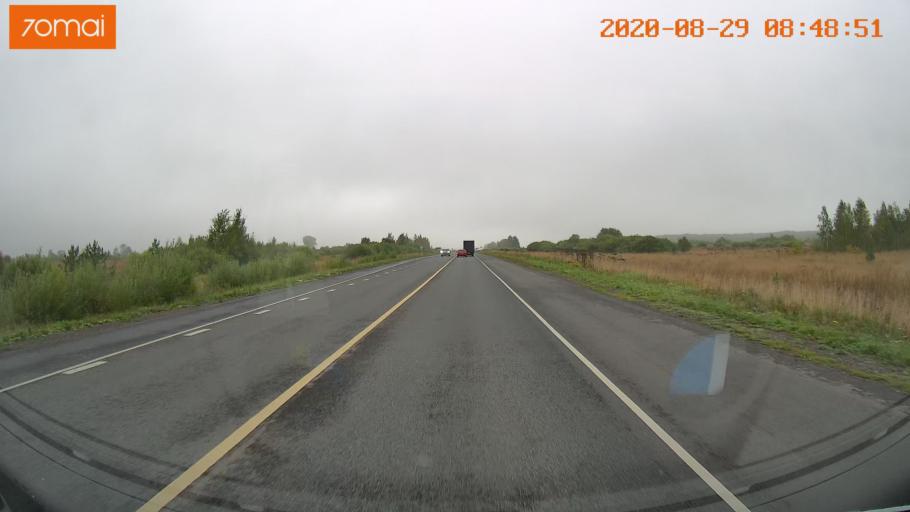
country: RU
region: Ivanovo
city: Vichuga
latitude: 57.1657
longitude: 41.8567
